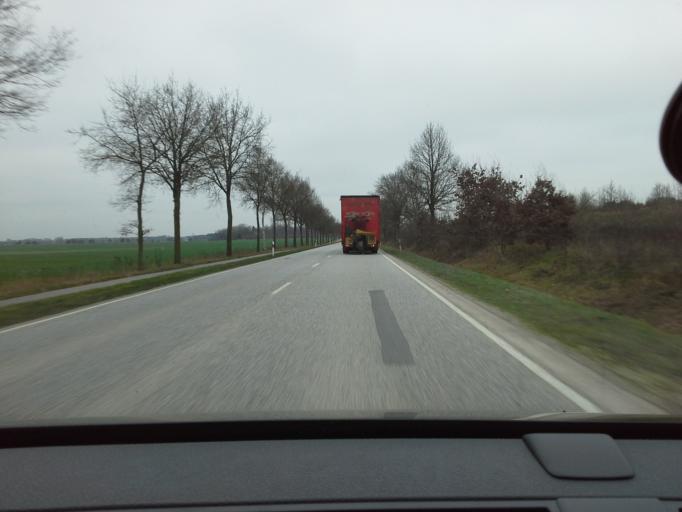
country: DE
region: Schleswig-Holstein
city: Lentfohrden
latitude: 53.8505
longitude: 9.8877
